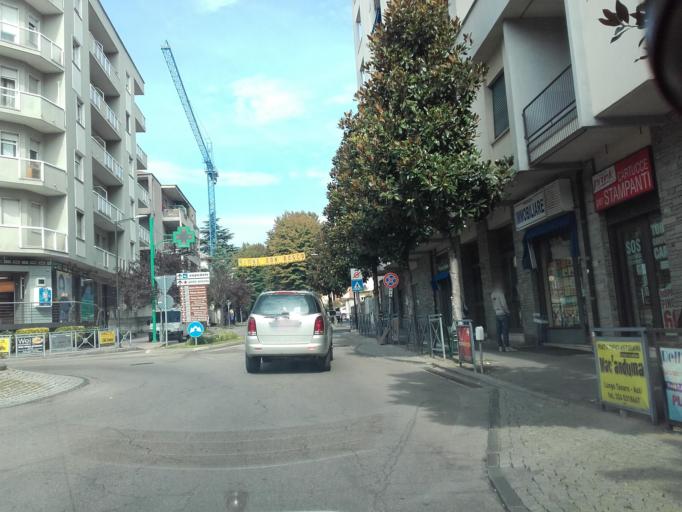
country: IT
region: Piedmont
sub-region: Provincia di Asti
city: Asti
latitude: 44.9058
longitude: 8.2024
